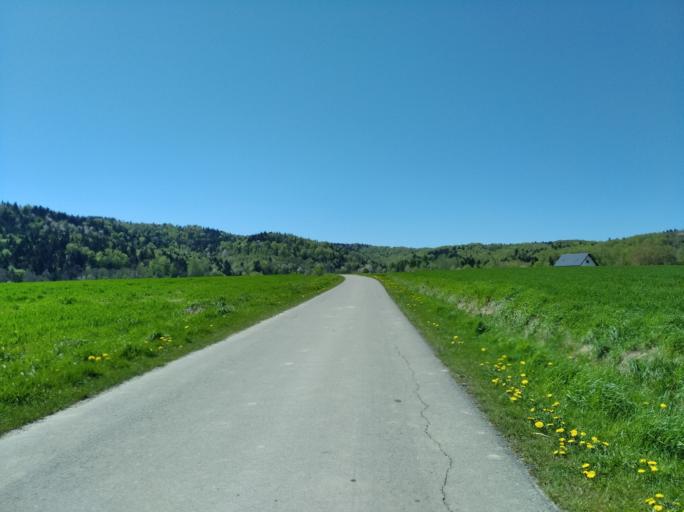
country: PL
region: Subcarpathian Voivodeship
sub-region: Powiat ropczycko-sedziszowski
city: Niedzwiada
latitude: 49.9076
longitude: 21.5379
